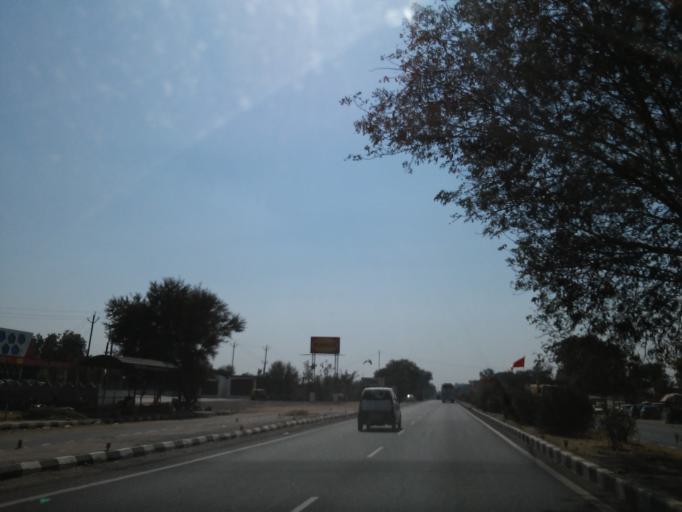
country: IN
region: Gujarat
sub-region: Gandhinagar
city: Chhala
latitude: 23.2864
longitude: 72.7623
